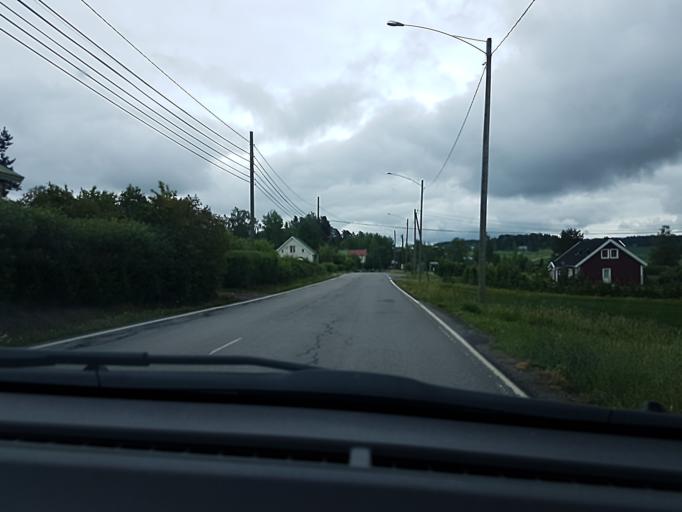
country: FI
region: Uusimaa
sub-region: Helsinki
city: Pornainen
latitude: 60.4334
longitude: 25.3963
